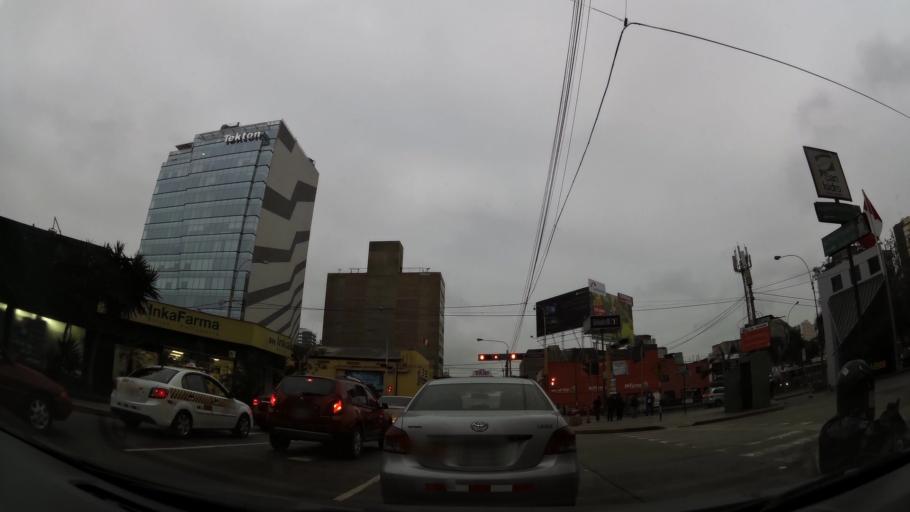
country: PE
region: Lima
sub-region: Lima
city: San Isidro
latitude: -12.0926
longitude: -77.0321
